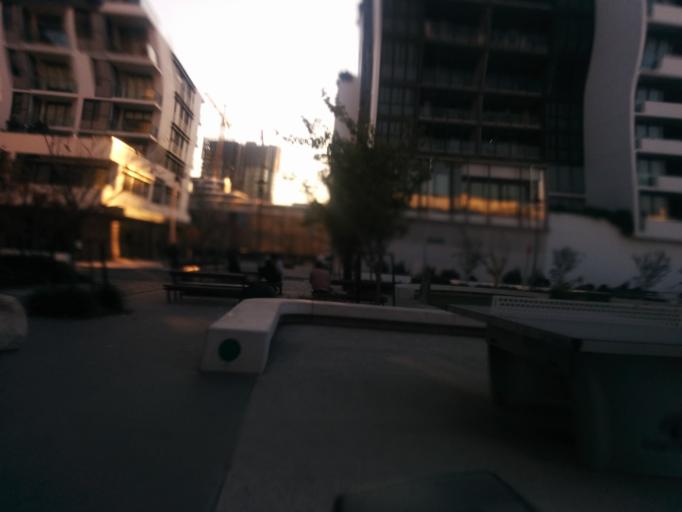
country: AU
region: New South Wales
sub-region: City of Sydney
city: Alexandria
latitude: -33.9030
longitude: 151.2137
